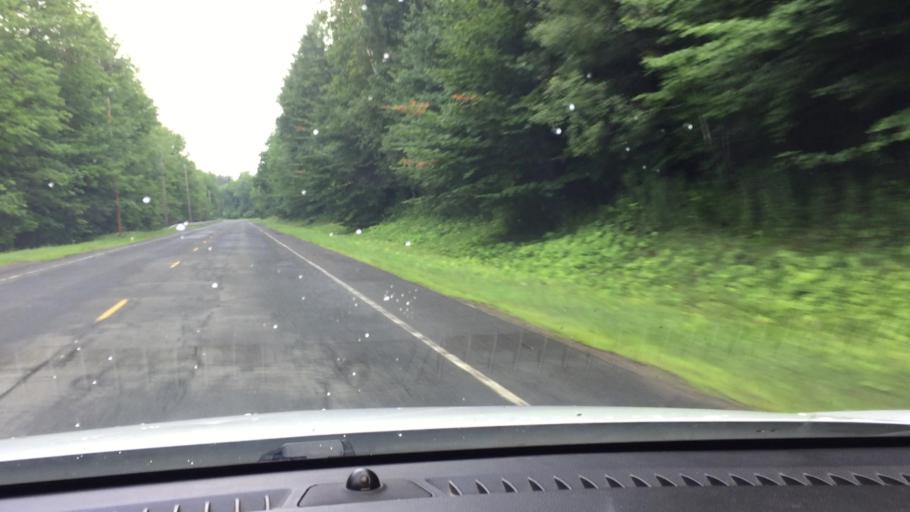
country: US
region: Massachusetts
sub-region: Berkshire County
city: Hinsdale
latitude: 42.4273
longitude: -73.0061
